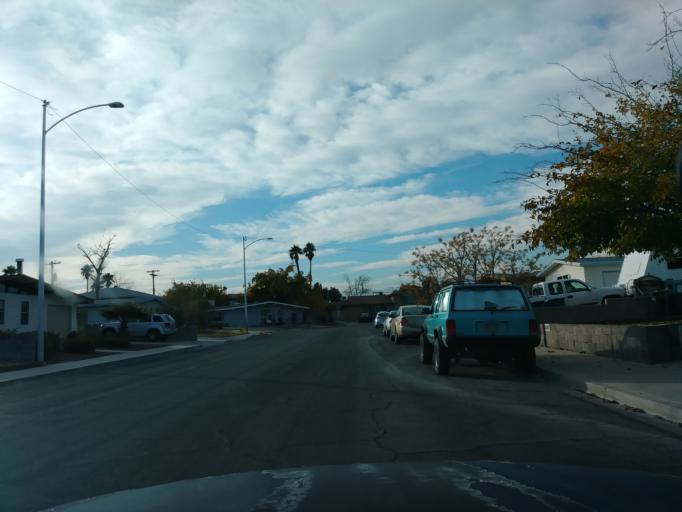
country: US
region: Nevada
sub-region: Clark County
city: Spring Valley
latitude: 36.1686
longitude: -115.2312
